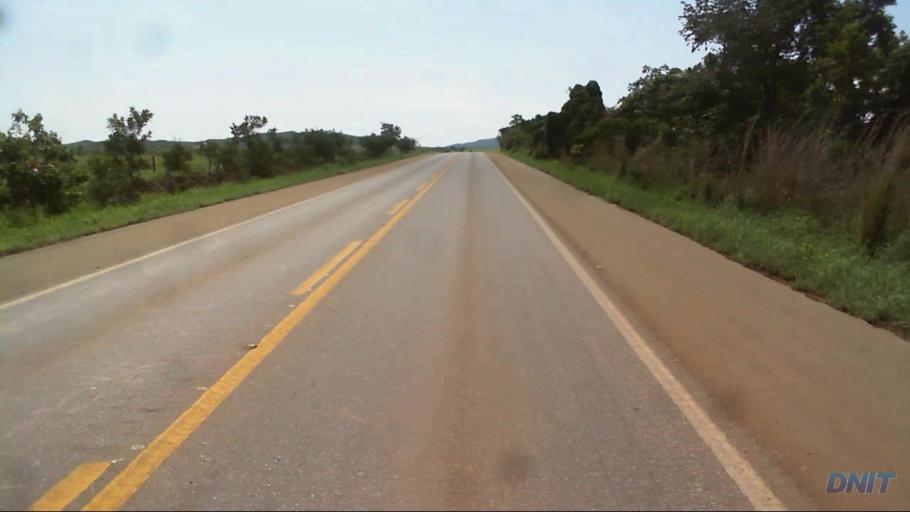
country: BR
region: Goias
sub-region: Barro Alto
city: Barro Alto
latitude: -15.1870
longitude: -48.7796
